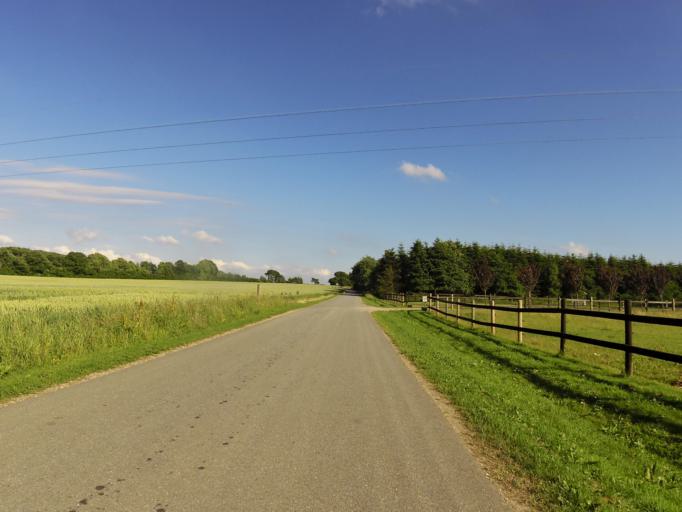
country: DK
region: South Denmark
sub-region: Vejen Kommune
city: Rodding
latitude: 55.3571
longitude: 9.0739
